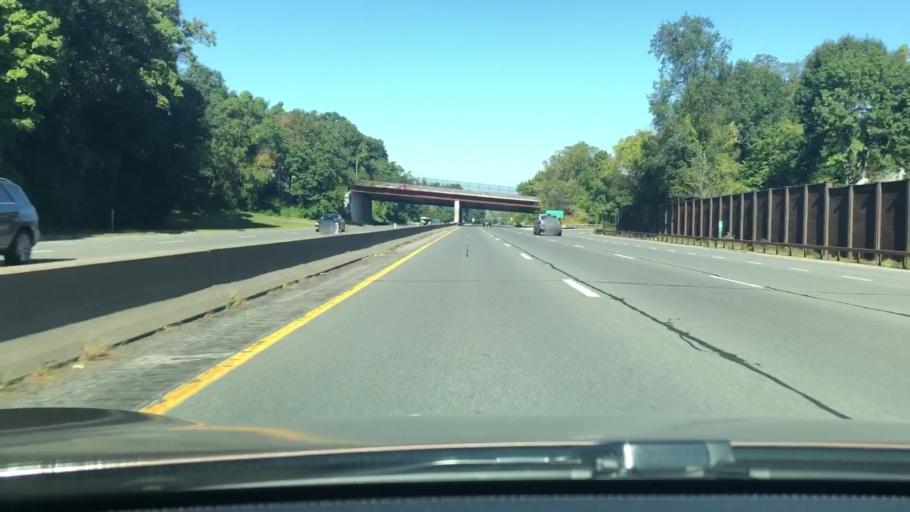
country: US
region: New York
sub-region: Westchester County
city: Bronxville
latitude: 40.9450
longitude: -73.8483
